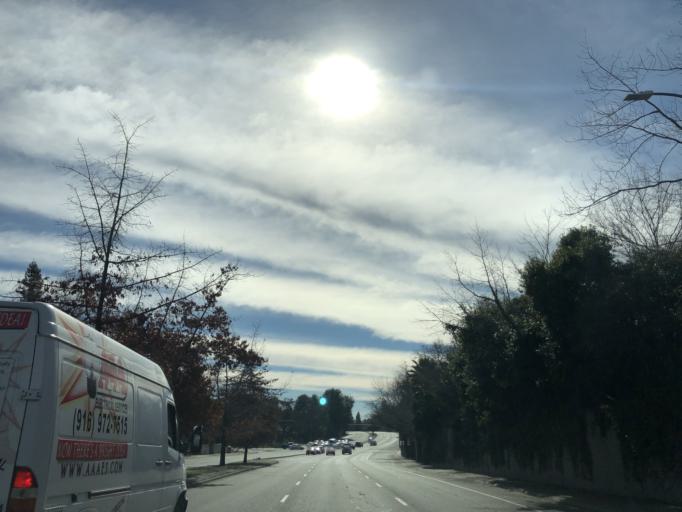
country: US
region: California
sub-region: Sacramento County
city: Fair Oaks
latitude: 38.6545
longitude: -121.2724
